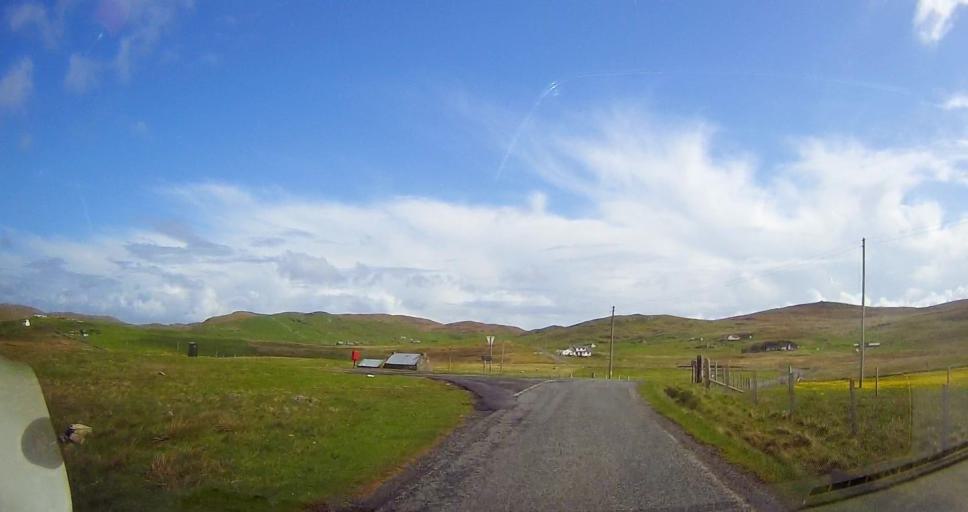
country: GB
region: Scotland
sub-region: Shetland Islands
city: Lerwick
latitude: 60.5898
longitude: -1.3334
